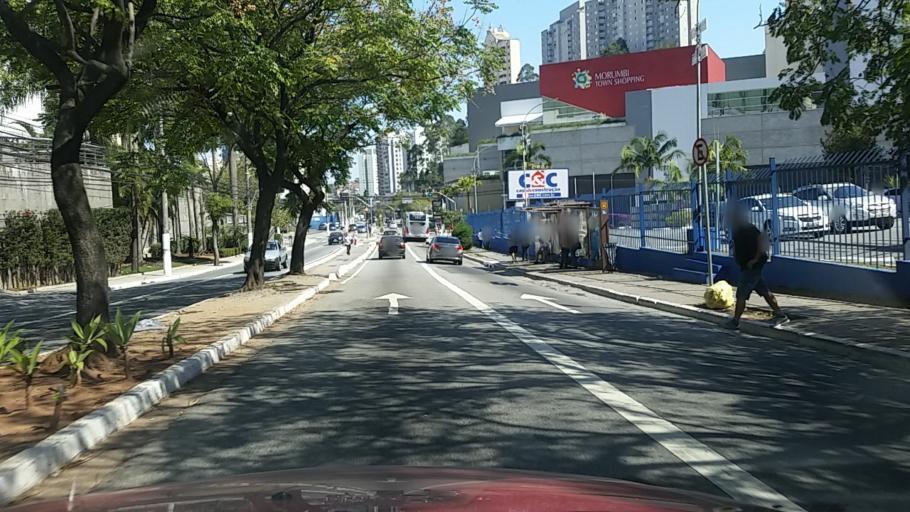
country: BR
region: Sao Paulo
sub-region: Taboao Da Serra
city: Taboao da Serra
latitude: -23.6305
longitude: -46.7365
